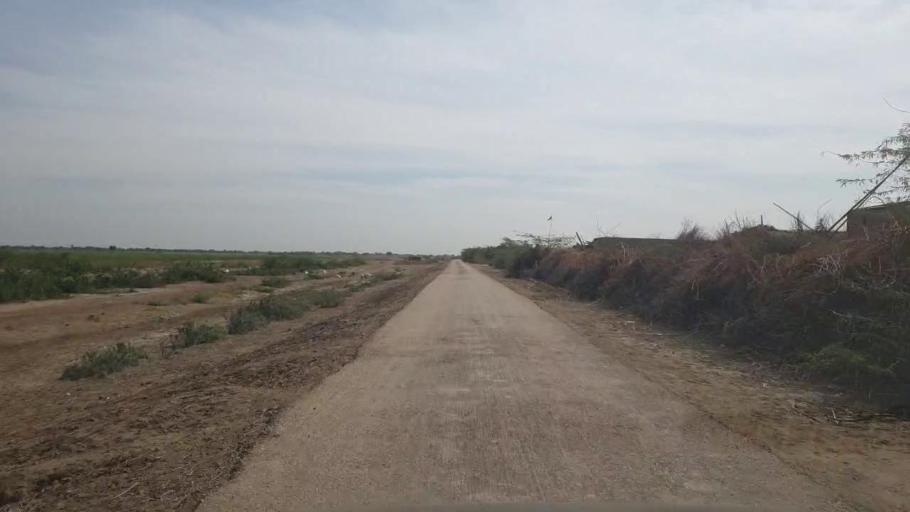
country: PK
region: Sindh
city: Kunri
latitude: 25.2712
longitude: 69.5999
